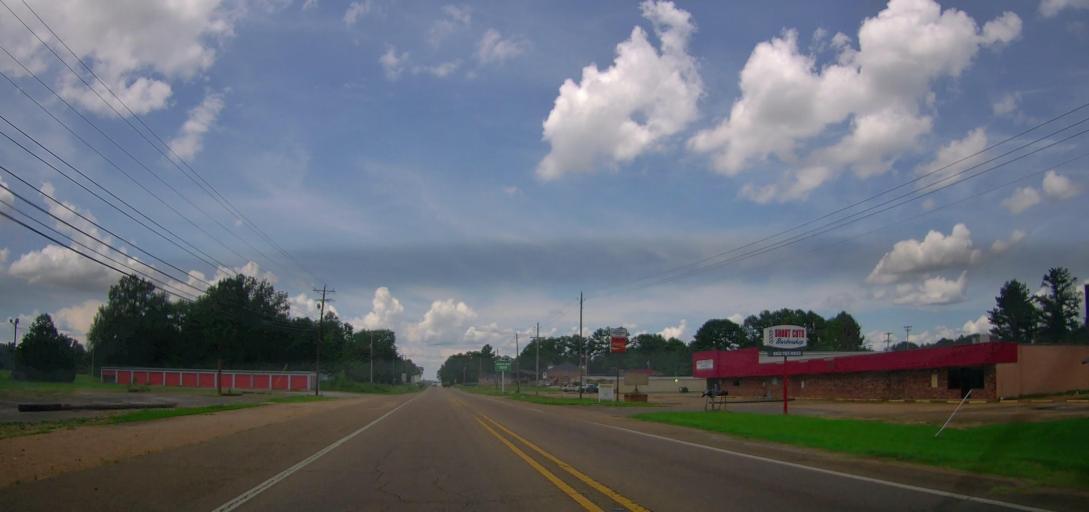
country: US
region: Mississippi
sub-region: Lee County
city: Shannon
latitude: 34.1274
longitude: -88.7193
